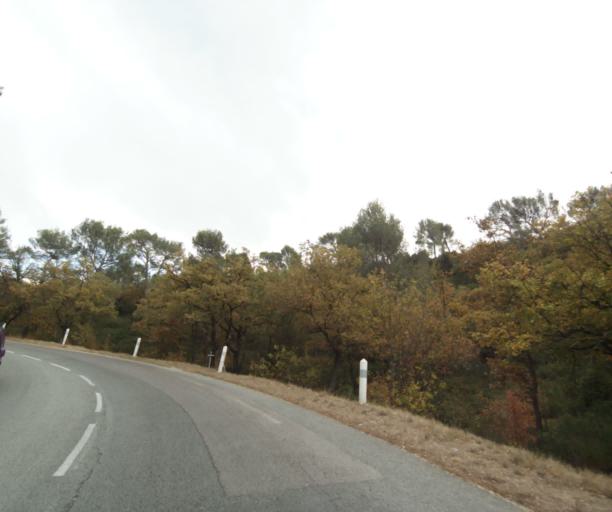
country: FR
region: Provence-Alpes-Cote d'Azur
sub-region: Departement des Bouches-du-Rhone
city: Cuges-les-Pins
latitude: 43.2658
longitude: 5.6619
